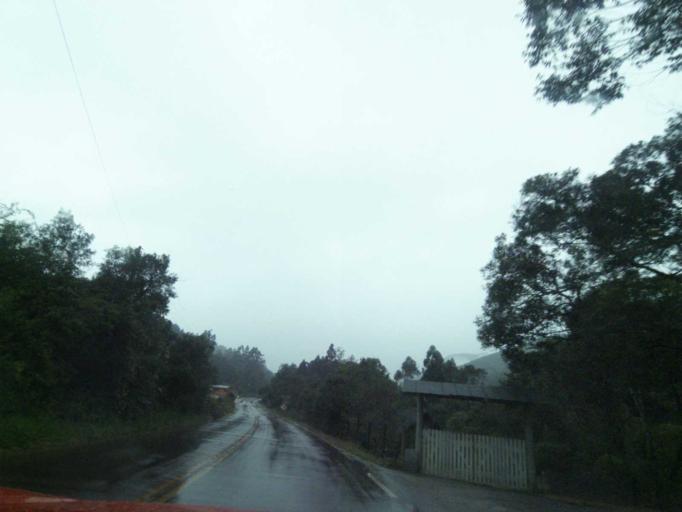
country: BR
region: Santa Catarina
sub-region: Anitapolis
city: Anitapolis
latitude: -27.8206
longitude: -49.0491
